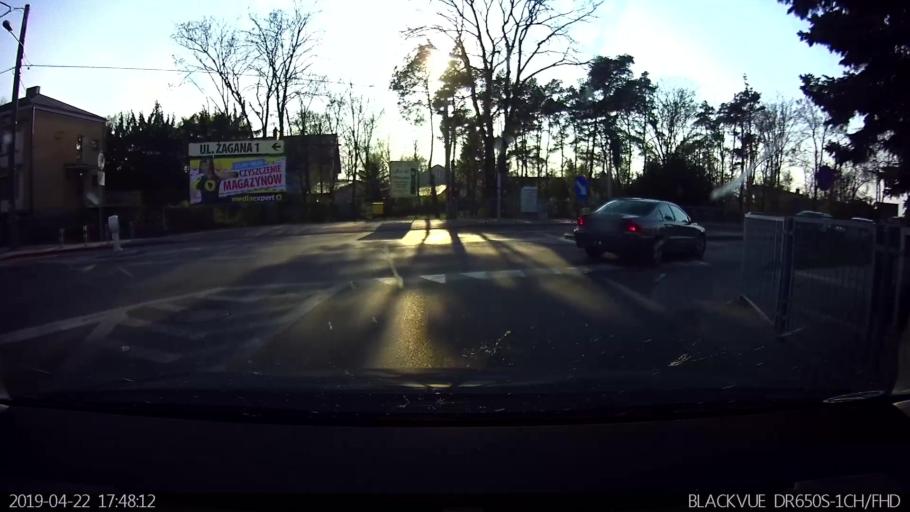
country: PL
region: Masovian Voivodeship
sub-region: Powiat wegrowski
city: Wegrow
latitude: 52.4042
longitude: 22.0154
